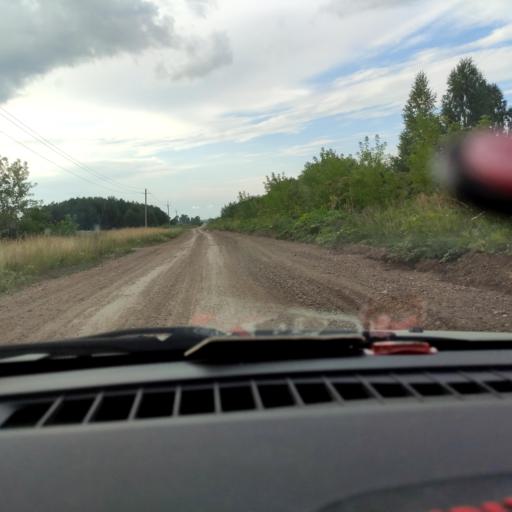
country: RU
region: Perm
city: Kultayevo
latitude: 57.8236
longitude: 55.9973
